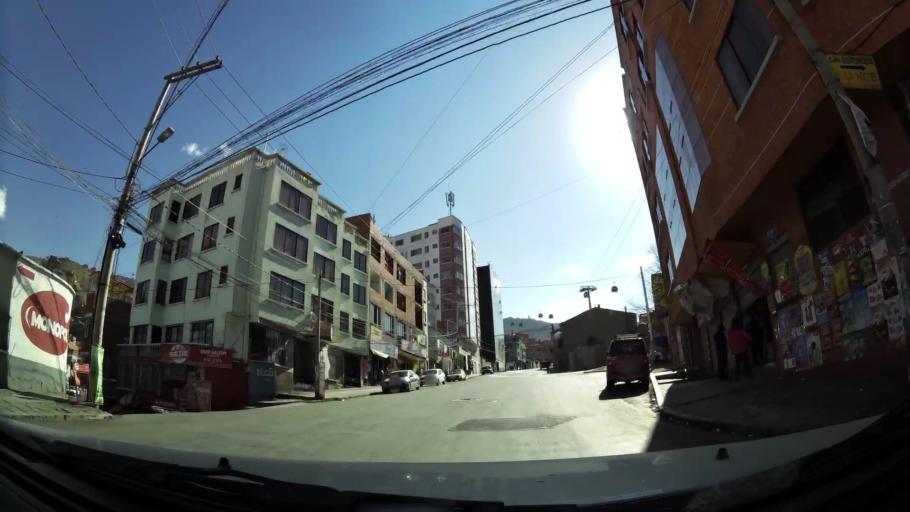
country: BO
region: La Paz
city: La Paz
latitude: -16.5156
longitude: -68.1343
